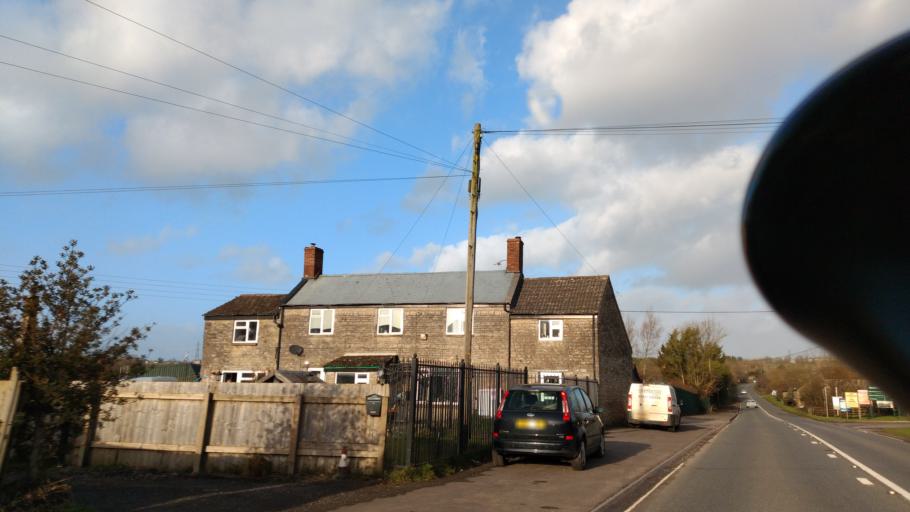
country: GB
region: England
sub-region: Somerset
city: Evercreech
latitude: 51.1497
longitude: -2.5455
